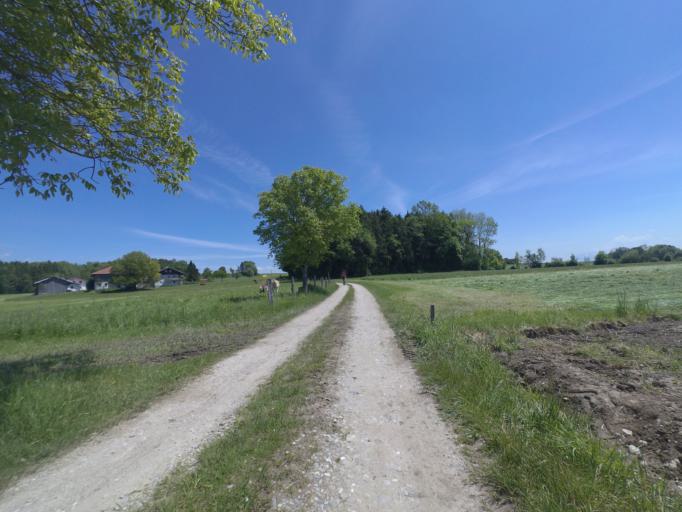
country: DE
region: Bavaria
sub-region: Upper Bavaria
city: Petting
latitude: 47.9486
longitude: 12.7863
